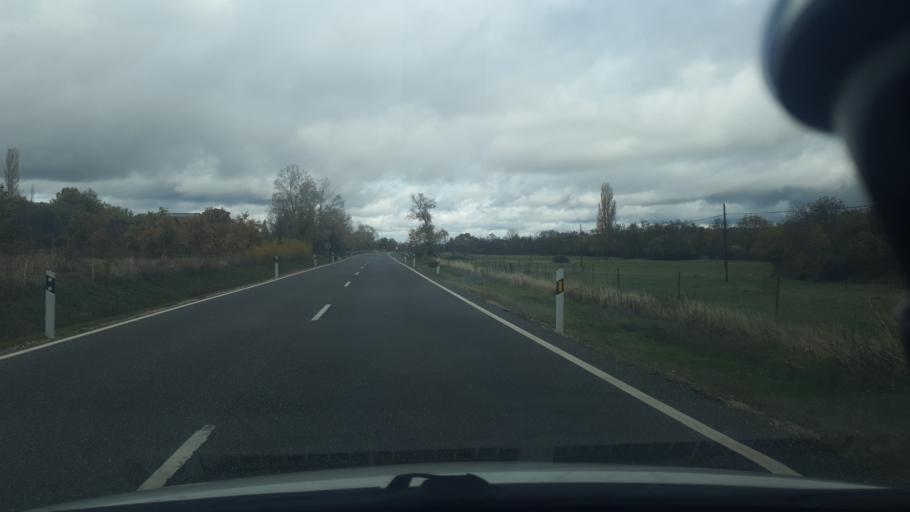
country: ES
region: Castille and Leon
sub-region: Provincia de Segovia
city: Collado Hermoso
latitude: 41.0471
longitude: -3.9121
